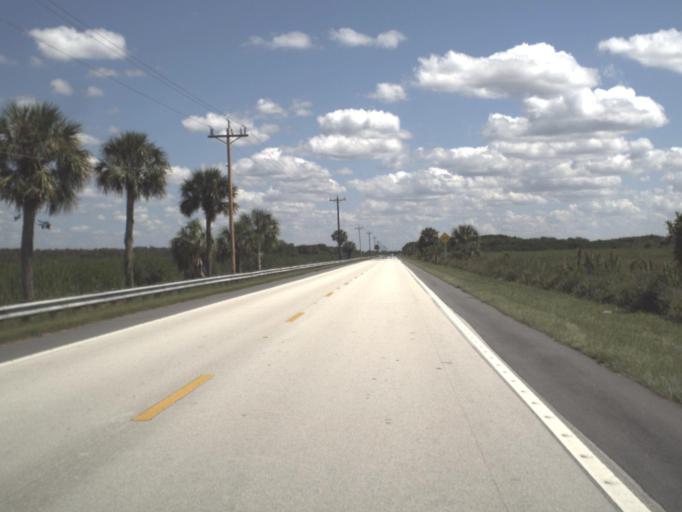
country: US
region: Florida
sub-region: Collier County
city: Marco
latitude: 25.9074
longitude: -81.3546
